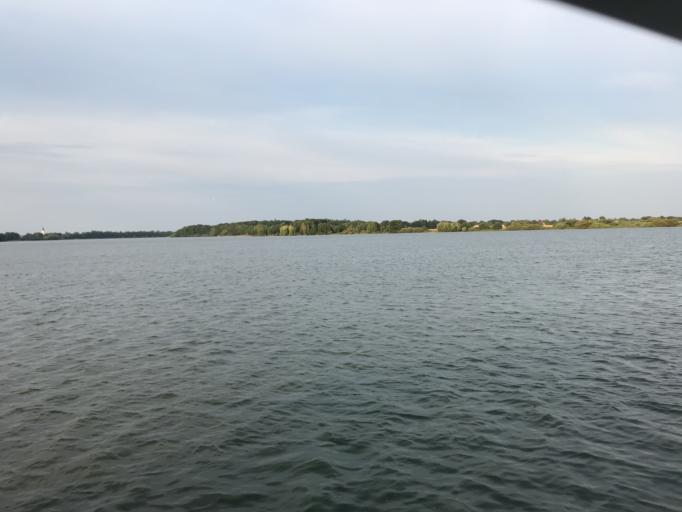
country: CZ
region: Jihocesky
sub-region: Okres Jindrichuv Hradec
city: Trebon
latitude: 48.9904
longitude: 14.7420
